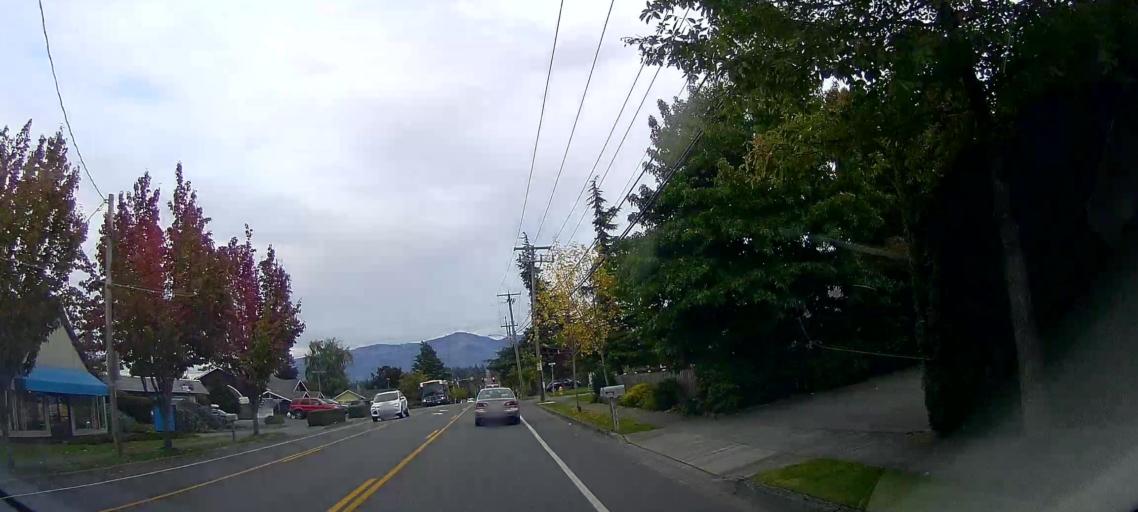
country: US
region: Washington
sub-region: Skagit County
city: Mount Vernon
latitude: 48.4210
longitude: -122.3214
